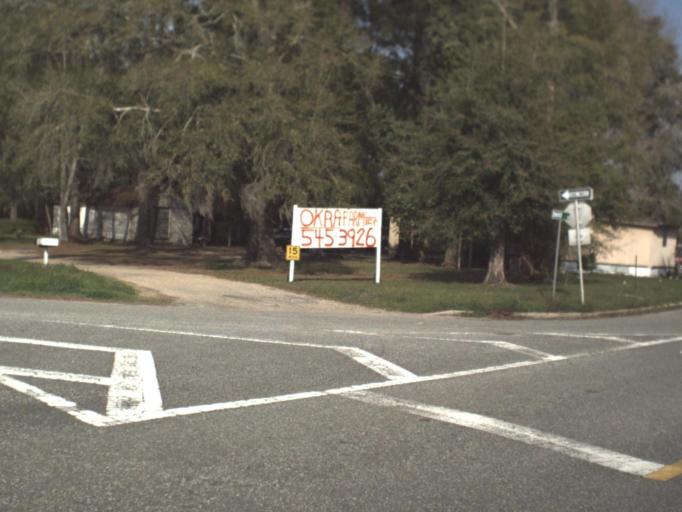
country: US
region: Florida
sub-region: Jefferson County
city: Monticello
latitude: 30.4909
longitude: -83.8818
